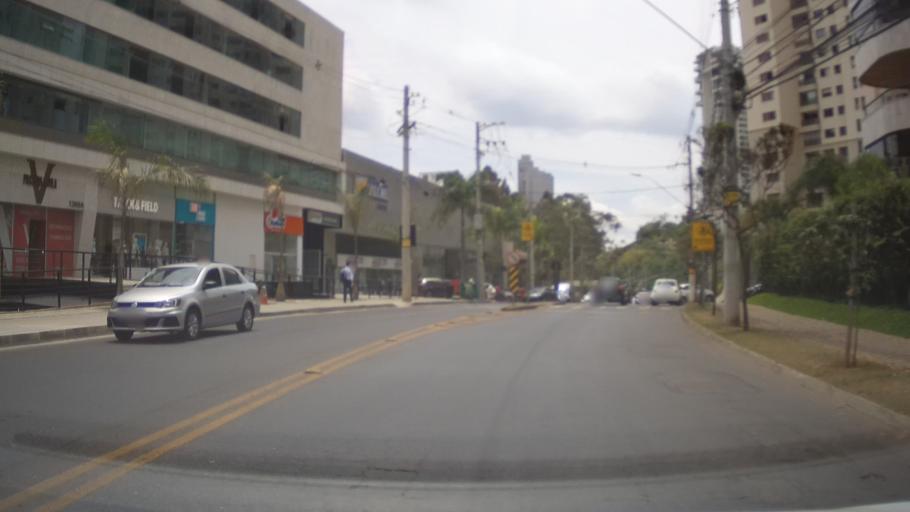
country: BR
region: Minas Gerais
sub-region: Belo Horizonte
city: Belo Horizonte
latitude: -19.9755
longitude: -43.9388
